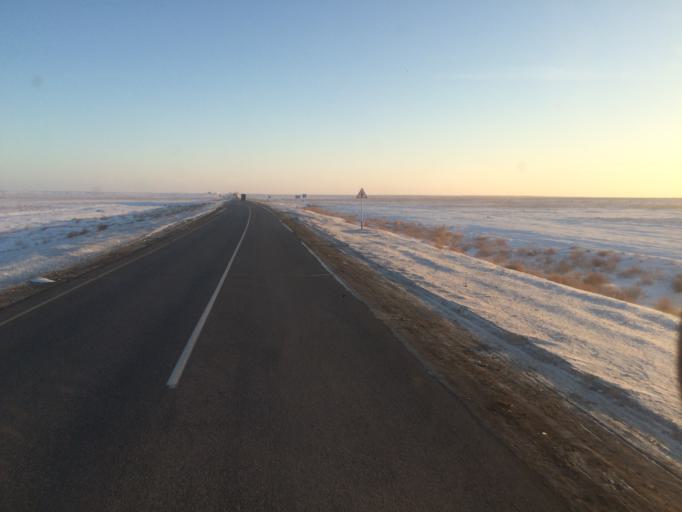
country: KZ
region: Qyzylorda
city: Sekseuil
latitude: 47.8212
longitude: 61.3394
